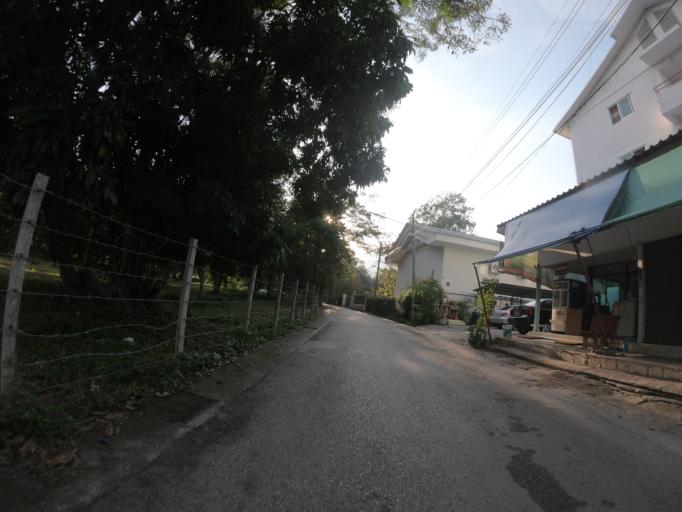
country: TH
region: Chiang Mai
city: Chiang Mai
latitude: 18.8159
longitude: 98.9567
